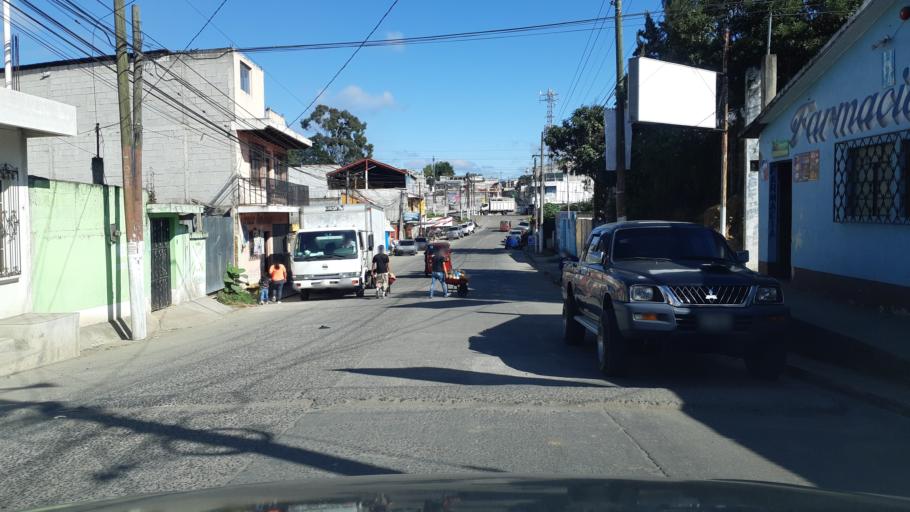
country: GT
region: Chimaltenango
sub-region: Municipio de Chimaltenango
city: Chimaltenango
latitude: 14.6577
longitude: -90.8219
